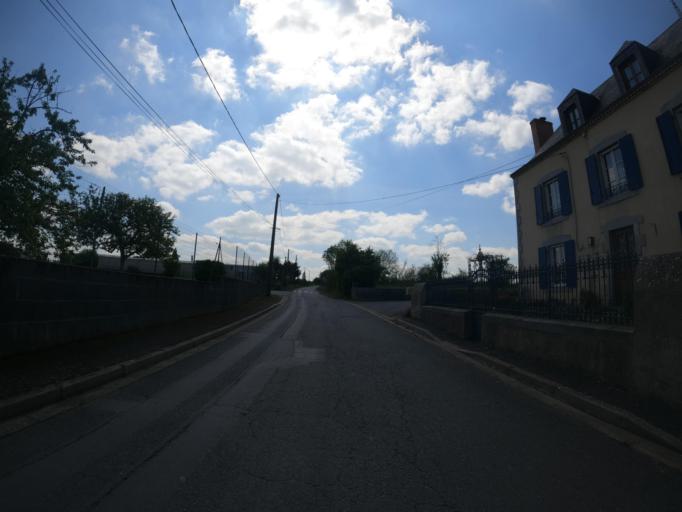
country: FR
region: Poitou-Charentes
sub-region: Departement des Deux-Sevres
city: Saint-Varent
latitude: 46.8588
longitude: -0.2530
